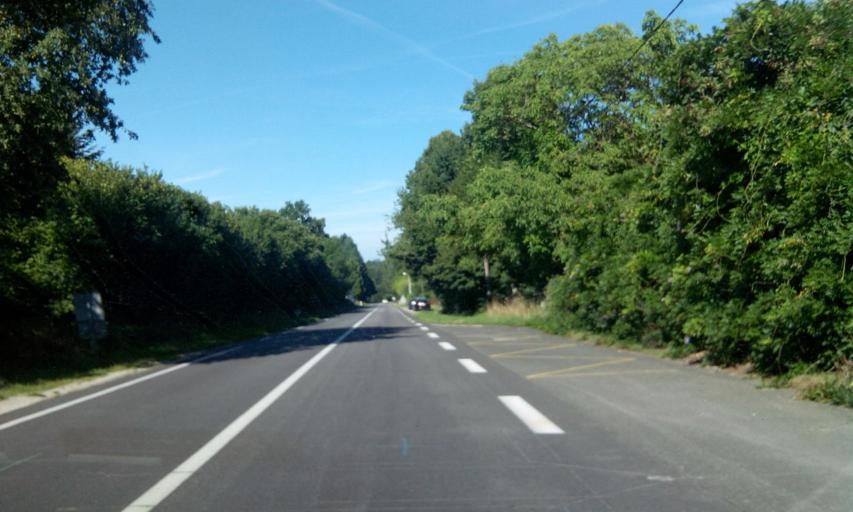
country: FR
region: Limousin
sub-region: Departement de la Haute-Vienne
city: Saint-Just-le-Martel
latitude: 45.8448
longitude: 1.4143
